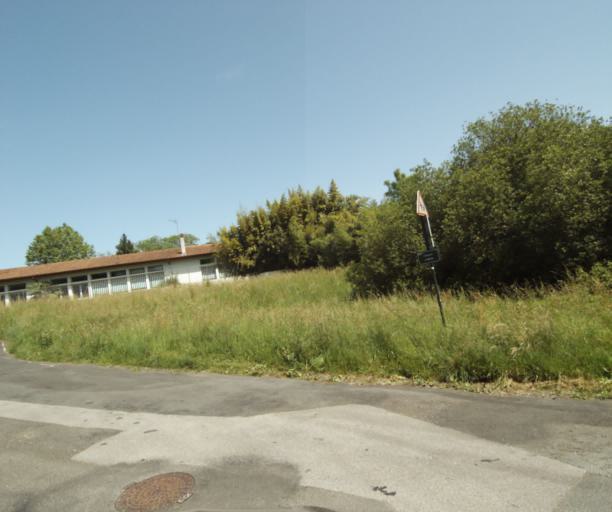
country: FR
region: Aquitaine
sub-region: Departement des Pyrenees-Atlantiques
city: Bayonne
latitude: 43.4808
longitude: -1.4573
